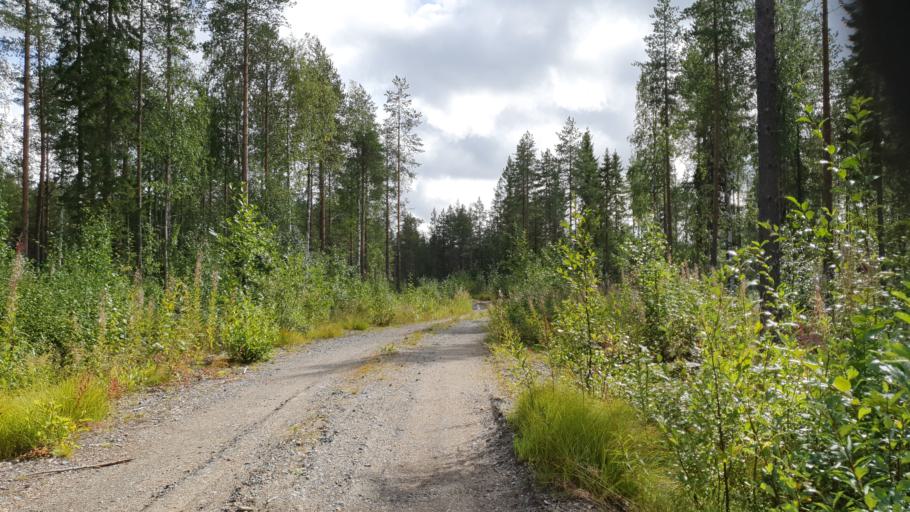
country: FI
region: Kainuu
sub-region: Kehys-Kainuu
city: Kuhmo
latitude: 64.1405
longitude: 29.3880
